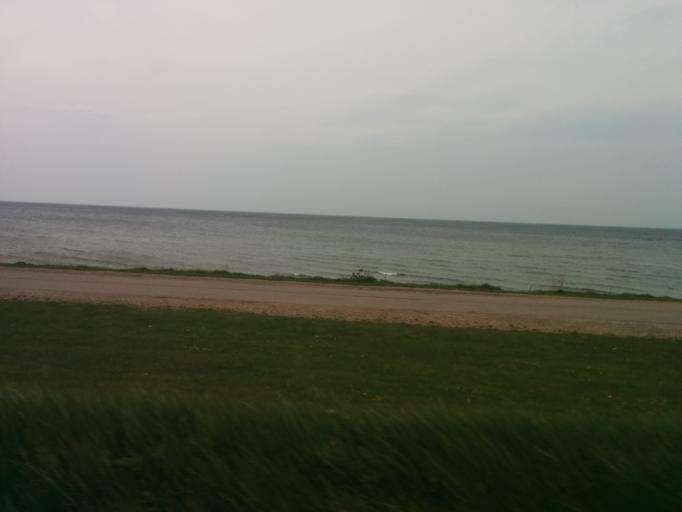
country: DK
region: Zealand
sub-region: Odsherred Kommune
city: Asnaes
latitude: 55.9608
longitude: 11.4323
